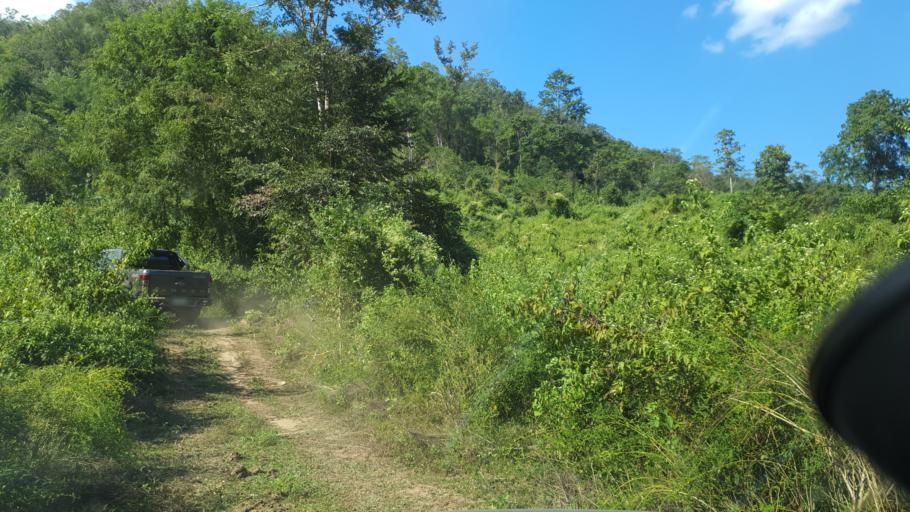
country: TH
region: Mae Hong Son
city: Mae Hi
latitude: 19.3060
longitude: 98.6997
